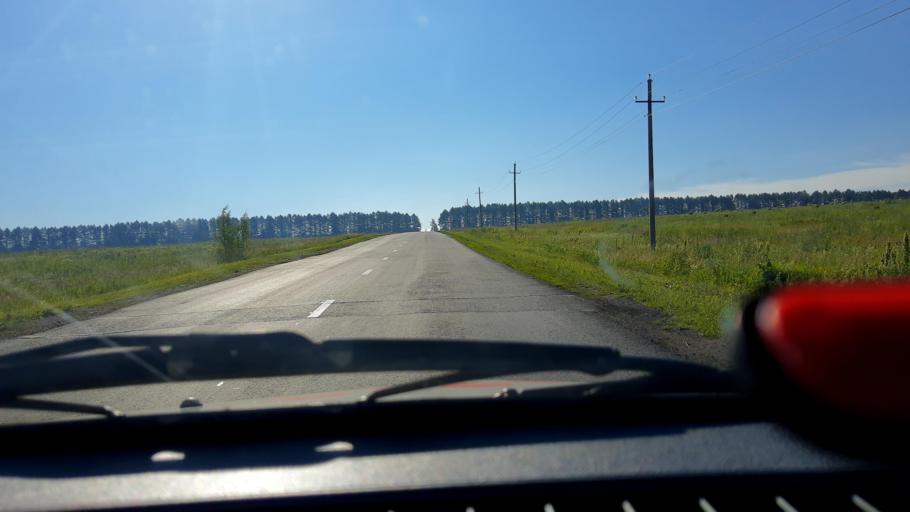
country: RU
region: Bashkortostan
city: Iglino
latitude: 54.7398
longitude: 56.2476
